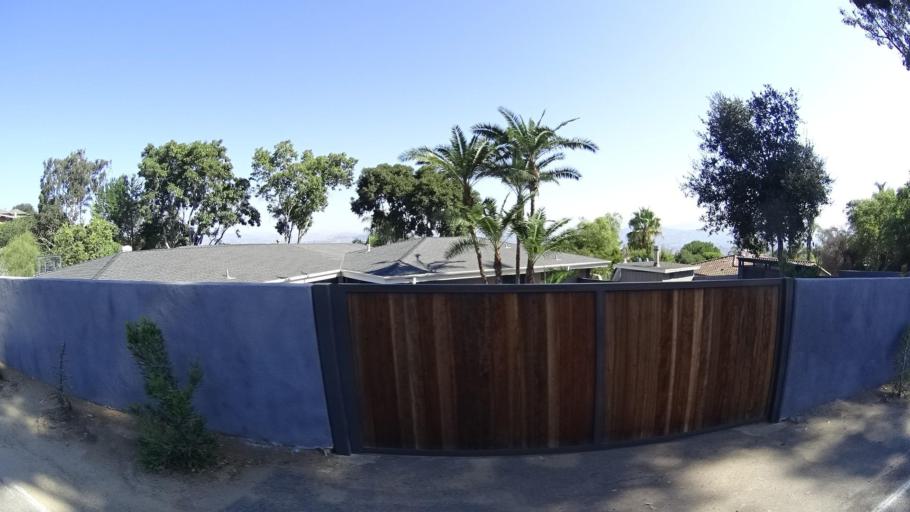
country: US
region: California
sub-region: San Diego County
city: Casa de Oro-Mount Helix
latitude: 32.7744
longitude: -116.9813
